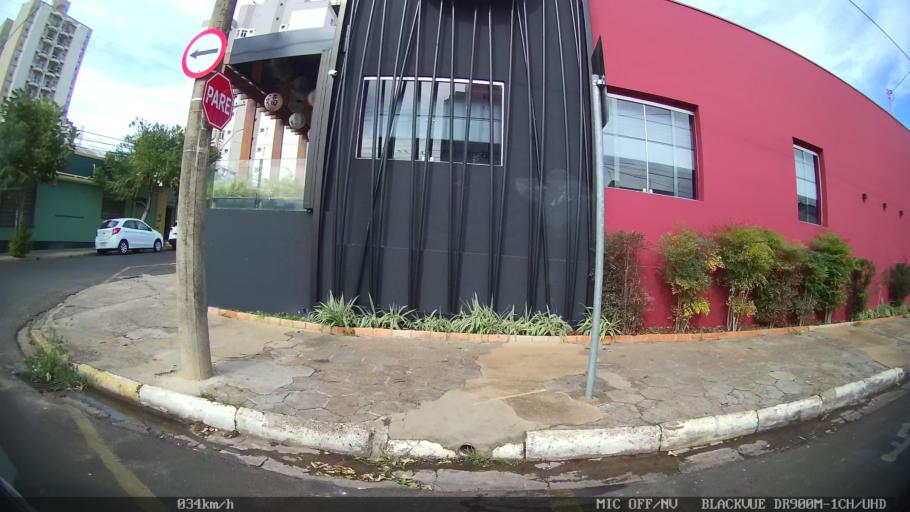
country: BR
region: Sao Paulo
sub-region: Catanduva
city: Catanduva
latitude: -21.1388
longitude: -48.9756
